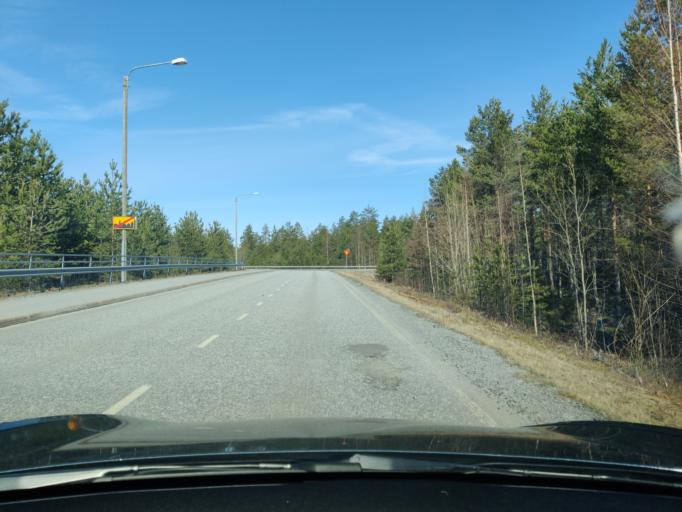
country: FI
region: Northern Savo
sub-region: Kuopio
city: Vehmersalmi
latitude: 62.7703
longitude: 28.0085
